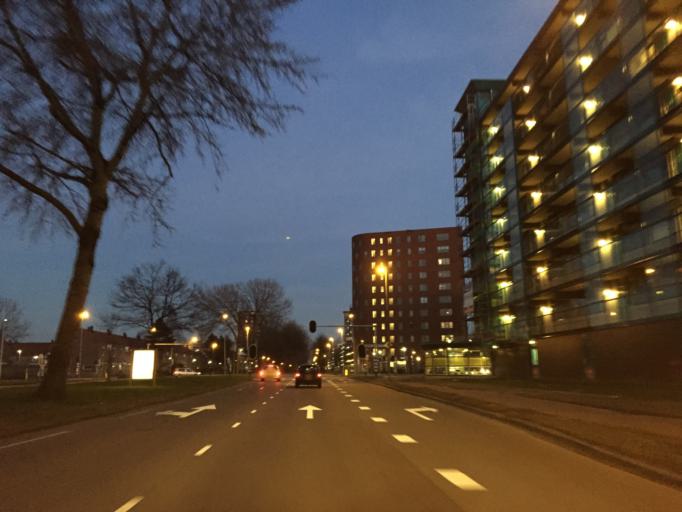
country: NL
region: South Holland
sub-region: Gemeente Leiderdorp
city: Leiderdorp
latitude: 52.1668
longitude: 4.5240
